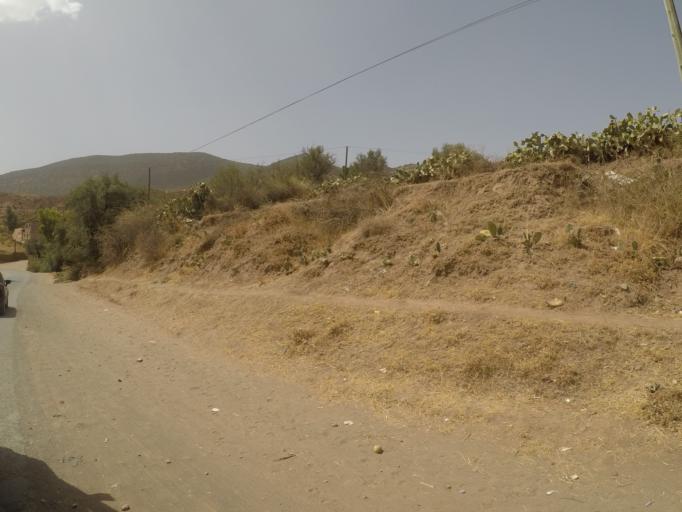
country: MA
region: Marrakech-Tensift-Al Haouz
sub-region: Al-Haouz
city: Moulay Brahim
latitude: 31.2360
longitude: -7.9760
